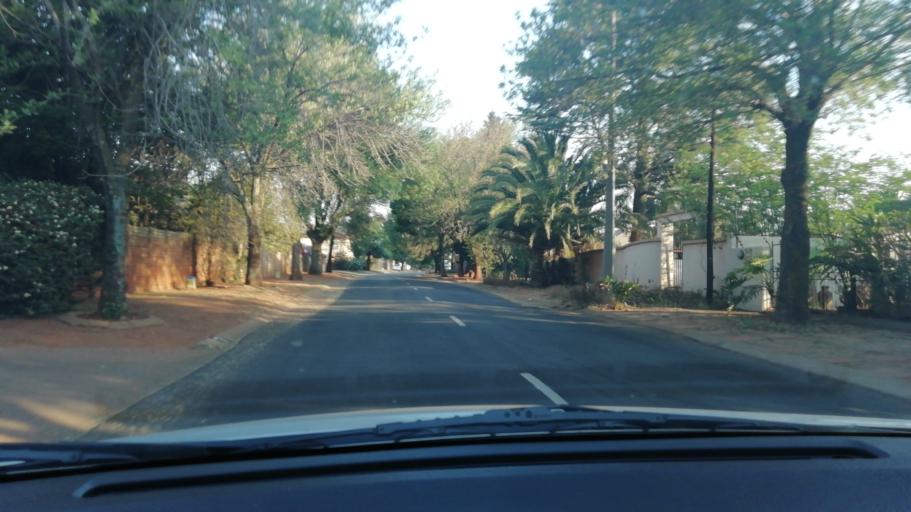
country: ZA
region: Gauteng
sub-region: Ekurhuleni Metropolitan Municipality
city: Benoni
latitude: -26.1998
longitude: 28.2925
